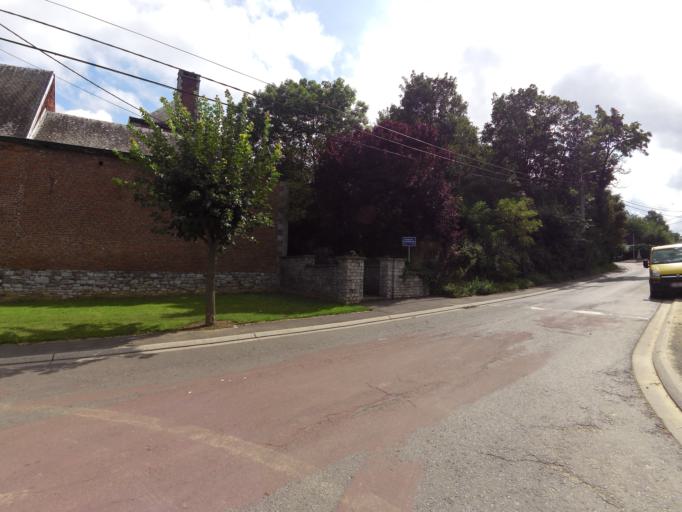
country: BE
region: Wallonia
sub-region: Province de Liege
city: Villers-le-Bouillet
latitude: 50.6135
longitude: 5.2319
